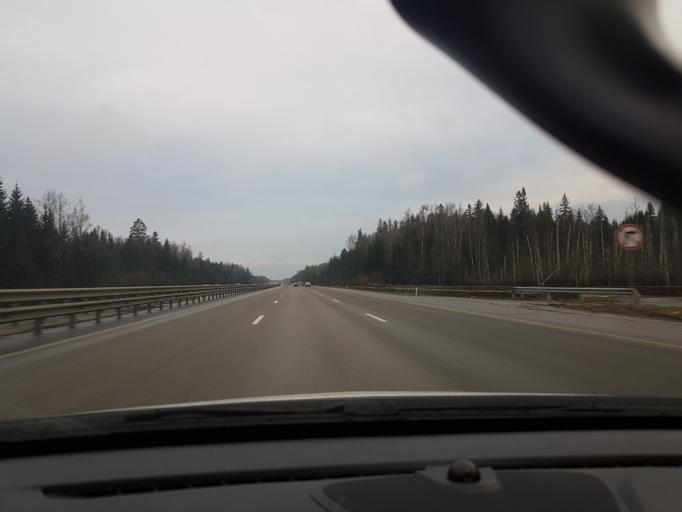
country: RU
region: Moskovskaya
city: Kostrovo
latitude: 55.9036
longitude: 36.6280
